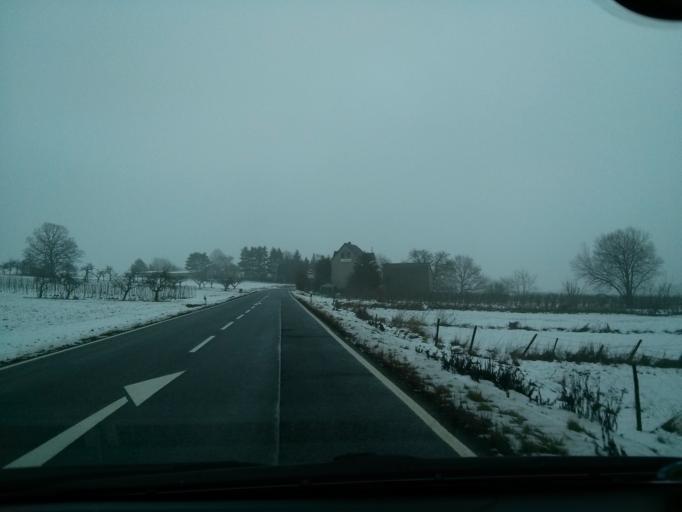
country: DE
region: Rheinland-Pfalz
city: Kalenborn
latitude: 50.5801
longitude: 6.9915
